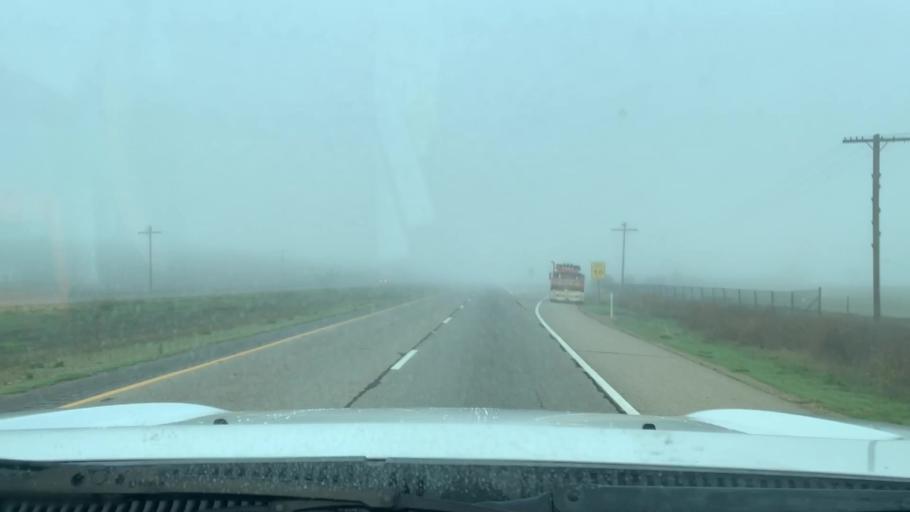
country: US
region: California
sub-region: San Luis Obispo County
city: Lake Nacimiento
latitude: 35.8705
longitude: -120.8295
